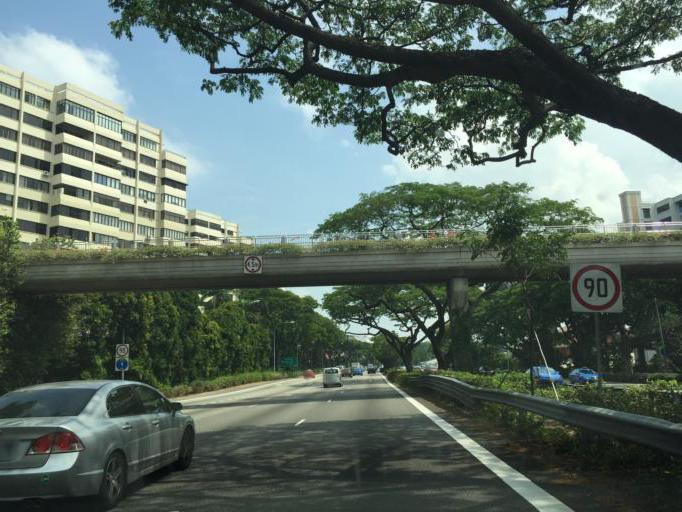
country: SG
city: Singapore
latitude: 1.3284
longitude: 103.9111
